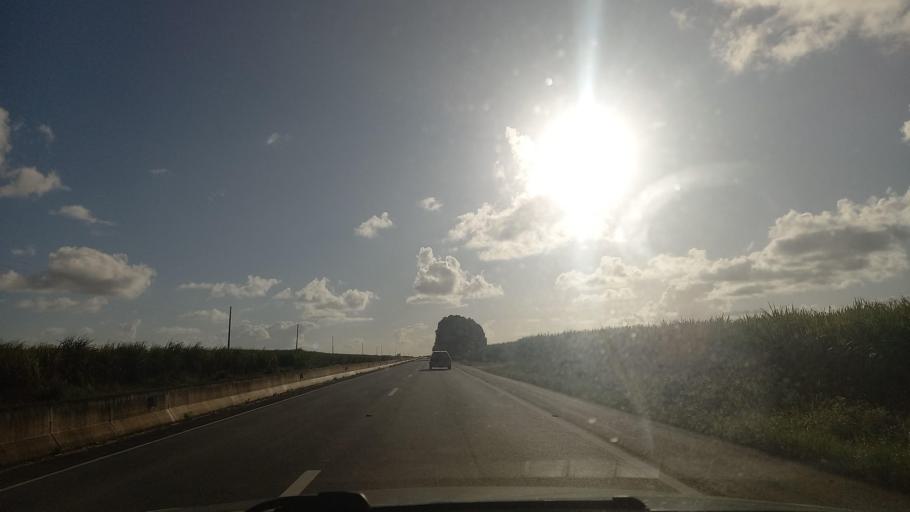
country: BR
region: Alagoas
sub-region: Sao Miguel Dos Campos
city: Sao Miguel dos Campos
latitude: -9.8010
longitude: -36.1563
